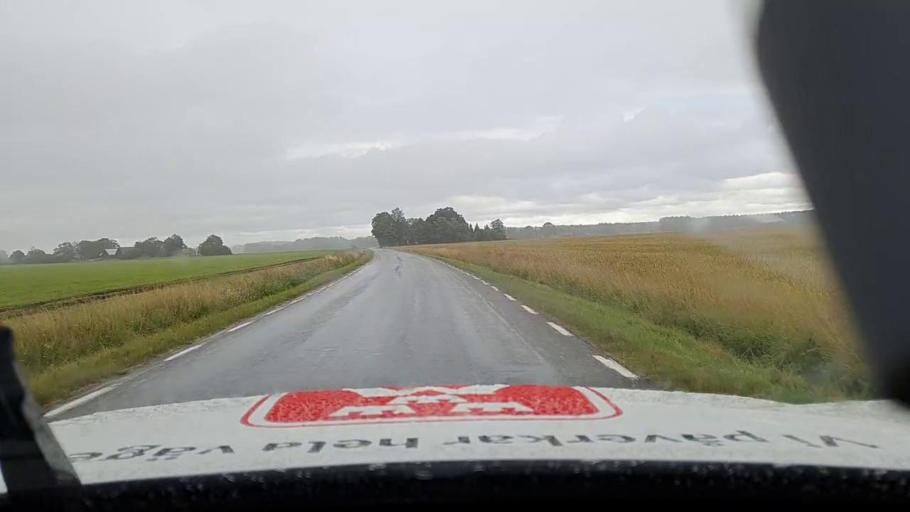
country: SE
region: Vaestra Goetaland
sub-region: Toreboda Kommun
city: Toereboda
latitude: 58.6548
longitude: 14.1096
